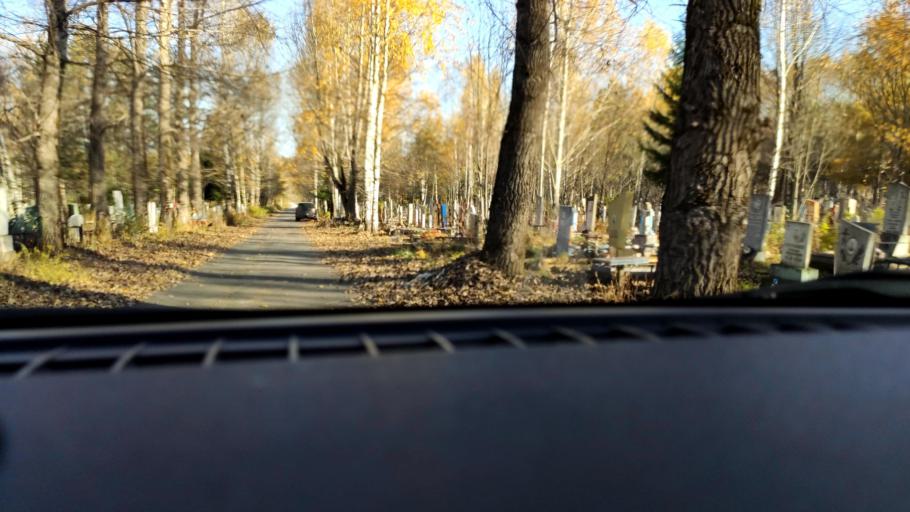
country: RU
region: Perm
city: Kondratovo
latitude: 58.0658
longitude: 56.1368
